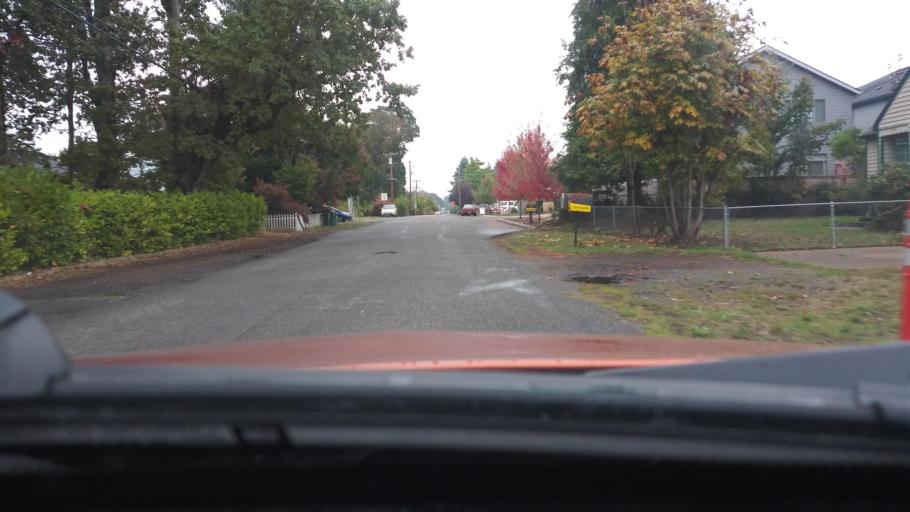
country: US
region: Oregon
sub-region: Washington County
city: Forest Grove
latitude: 45.5274
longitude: -123.1012
